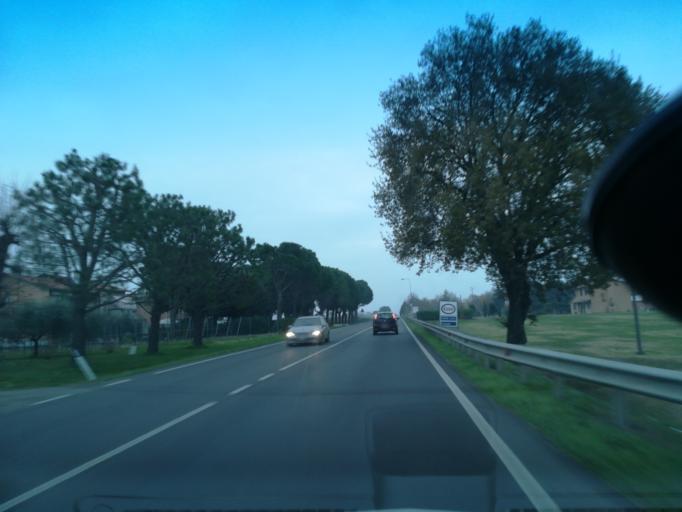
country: IT
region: Emilia-Romagna
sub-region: Provincia di Bologna
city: Imola
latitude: 44.3380
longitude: 11.7533
